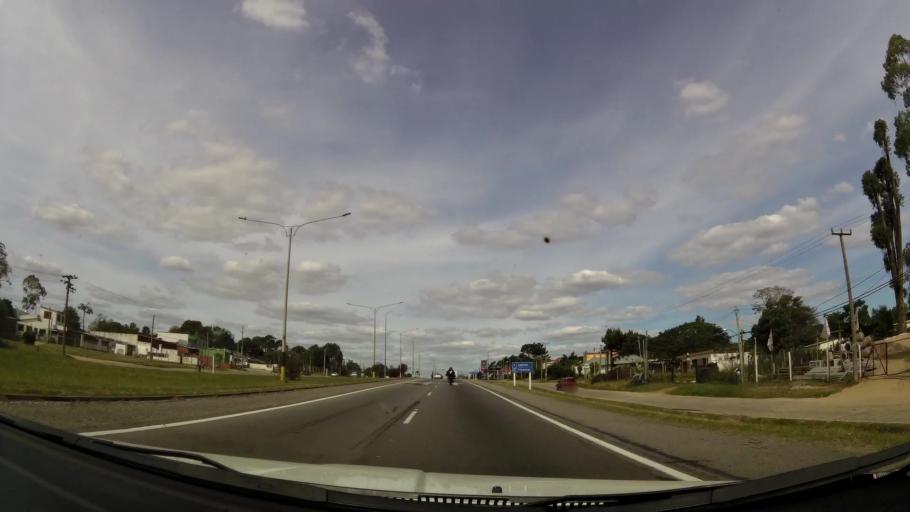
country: UY
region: Canelones
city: Empalme Olmos
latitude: -34.7790
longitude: -55.8653
